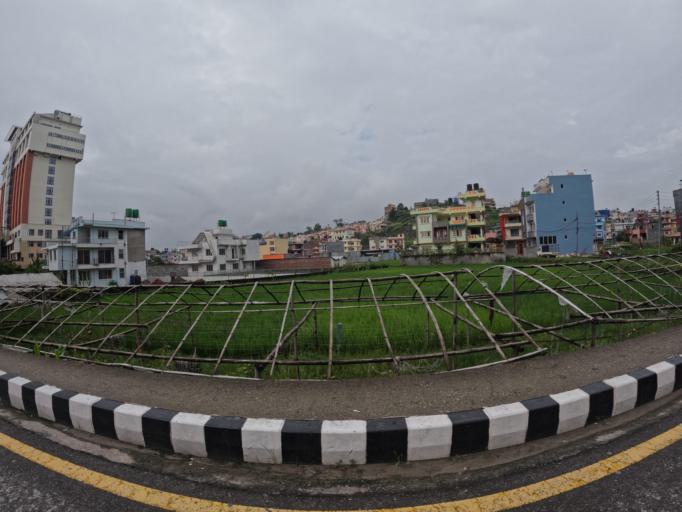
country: NP
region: Central Region
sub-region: Bagmati Zone
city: Kathmandu
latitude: 27.7542
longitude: 85.3256
